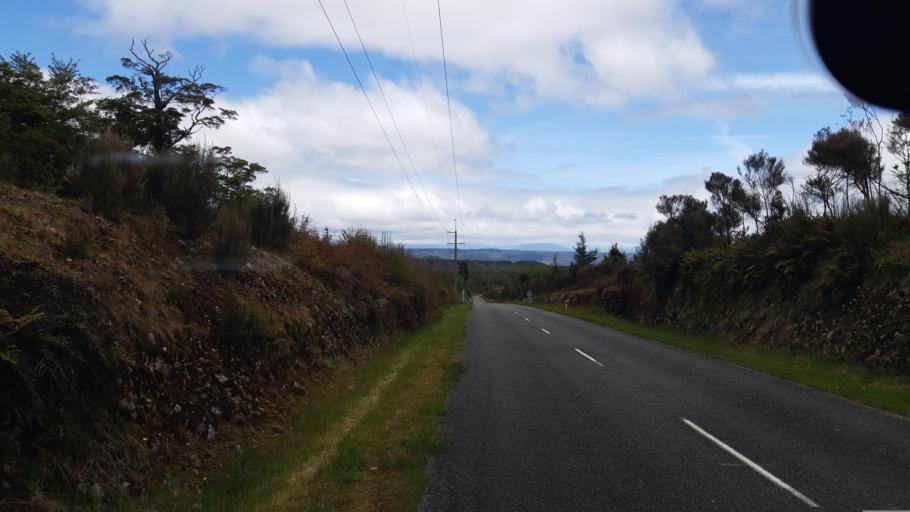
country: NZ
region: West Coast
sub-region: Grey District
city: Greymouth
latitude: -42.2594
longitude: 171.5465
